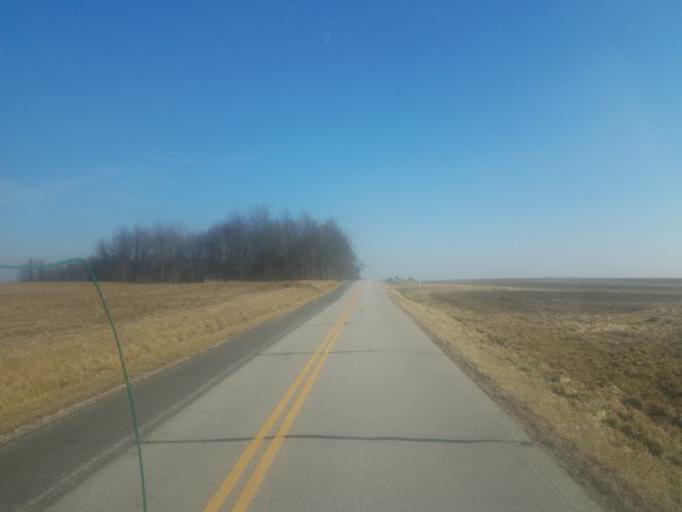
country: US
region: Ohio
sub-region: Crawford County
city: Bucyrus
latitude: 40.9066
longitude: -83.0686
